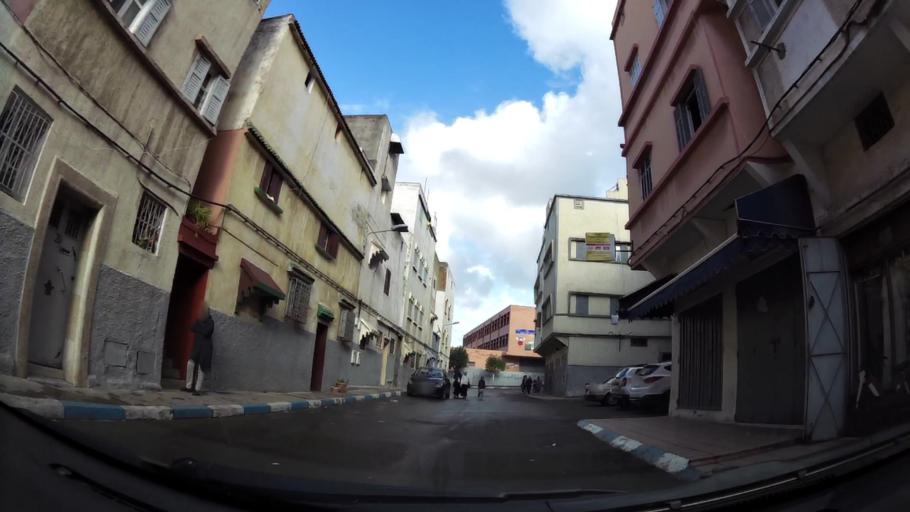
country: MA
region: Grand Casablanca
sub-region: Casablanca
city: Casablanca
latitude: 33.5501
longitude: -7.5958
